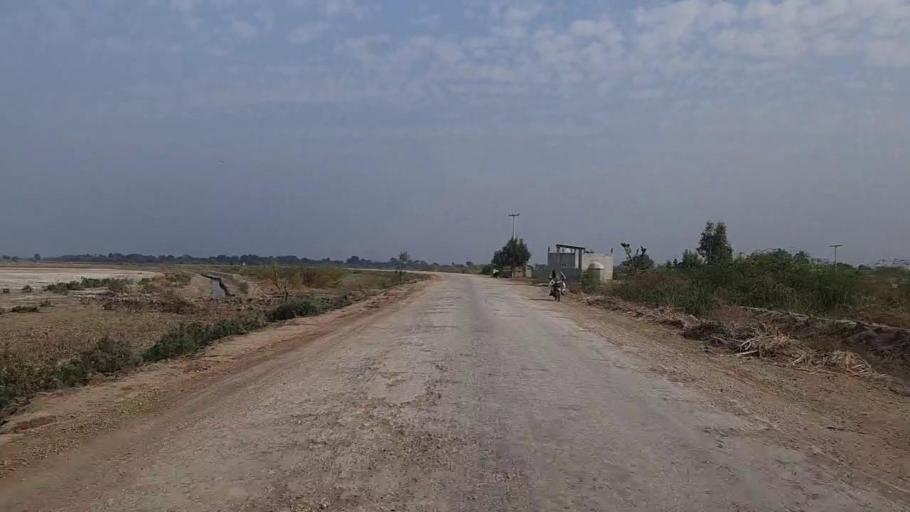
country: PK
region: Sindh
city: Mirwah Gorchani
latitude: 25.4052
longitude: 69.0471
